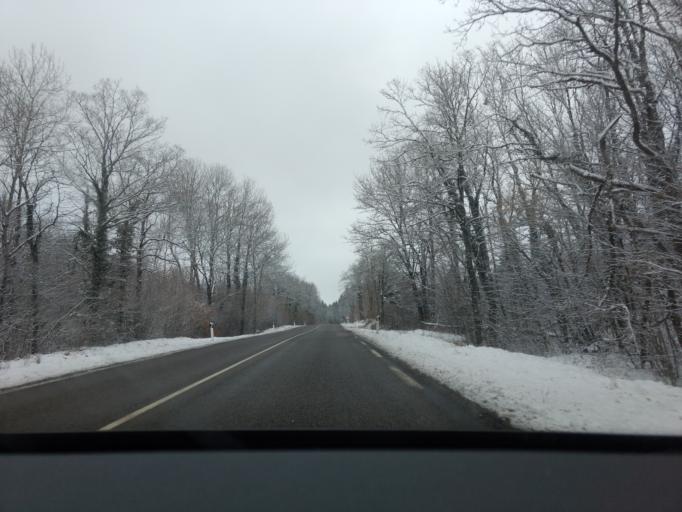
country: FR
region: Franche-Comte
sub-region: Departement du Jura
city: Champagnole
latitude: 46.7826
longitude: 5.8639
